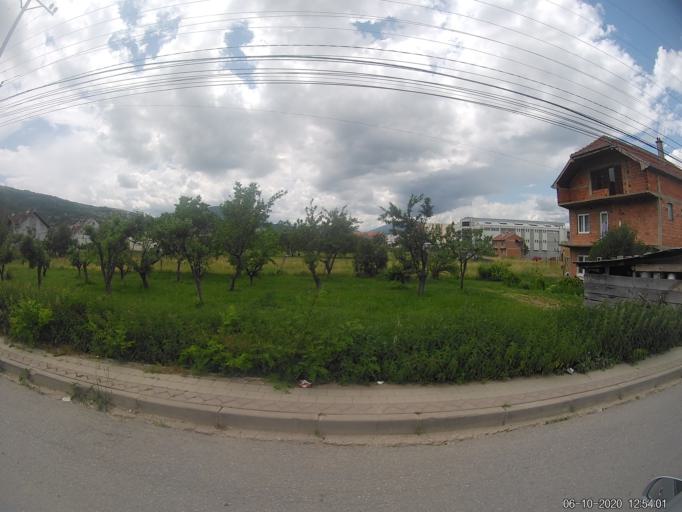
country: XK
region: Prizren
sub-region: Prizren
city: Prizren
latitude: 42.2387
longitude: 20.7673
